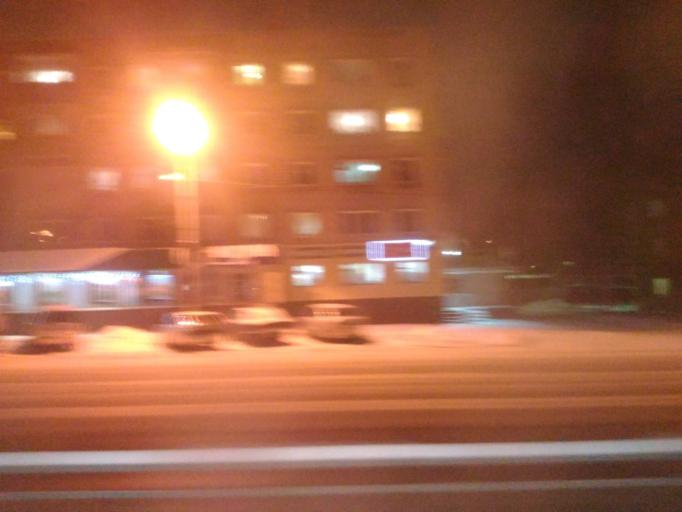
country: RU
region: Ulyanovsk
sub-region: Ulyanovskiy Rayon
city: Ulyanovsk
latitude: 54.3469
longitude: 48.3708
